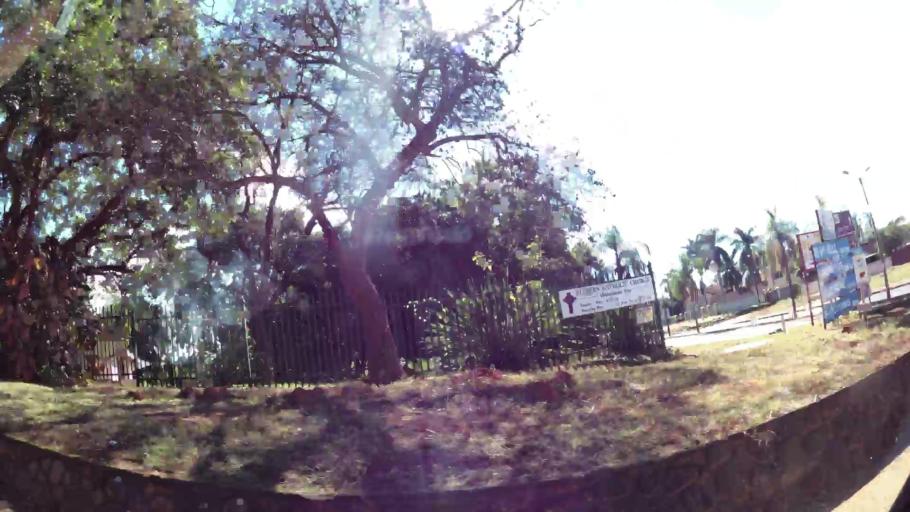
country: ZA
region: Limpopo
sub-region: Mopani District Municipality
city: Tzaneen
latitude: -23.8199
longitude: 30.1583
